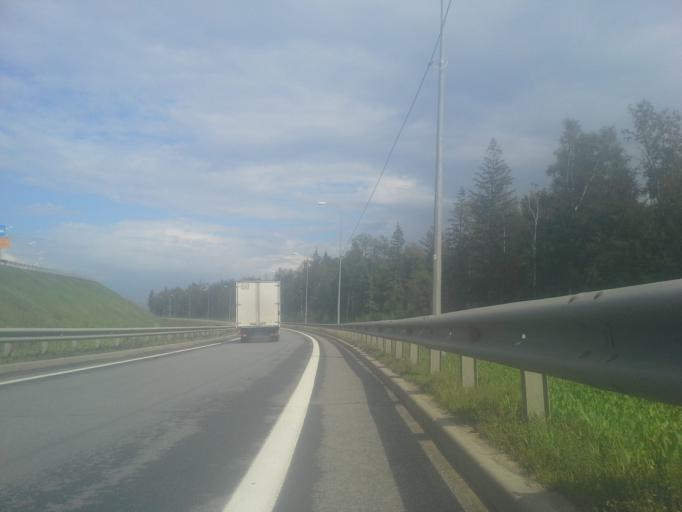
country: RU
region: Moskovskaya
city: Kokoshkino
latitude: 55.6235
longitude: 37.1708
